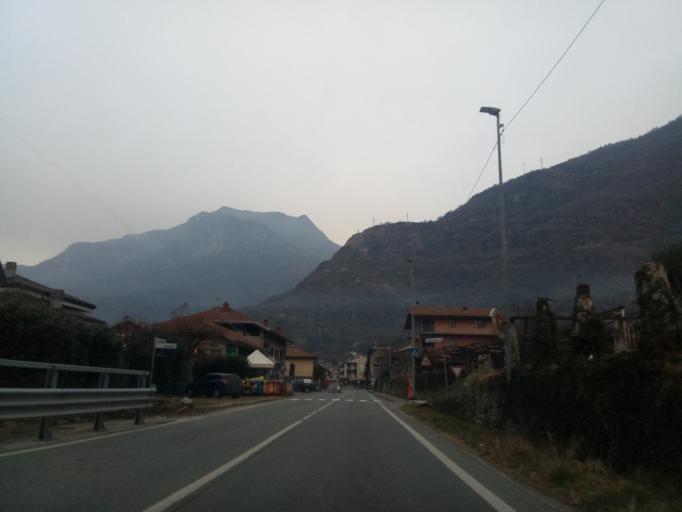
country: IT
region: Piedmont
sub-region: Provincia di Torino
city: Carema
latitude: 45.5810
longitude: 7.8085
